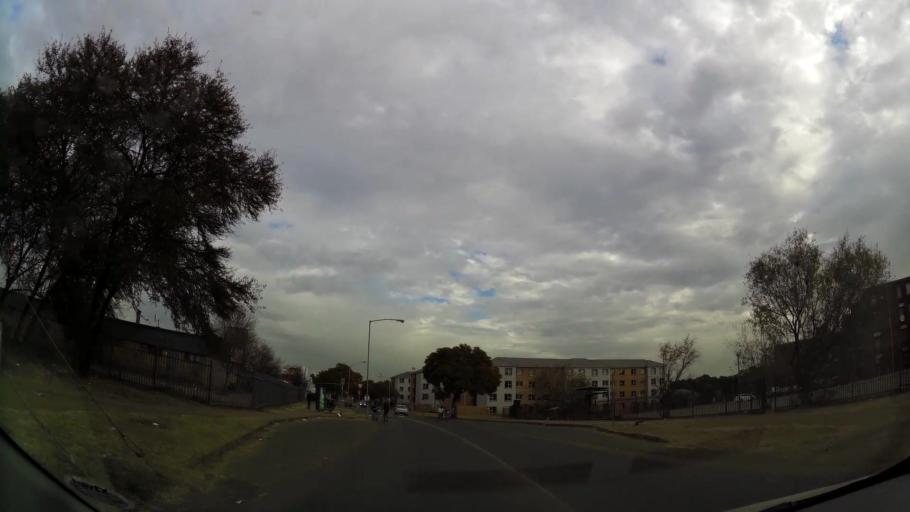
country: ZA
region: Gauteng
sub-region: City of Tshwane Metropolitan Municipality
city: Pretoria
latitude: -25.7072
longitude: 28.3085
